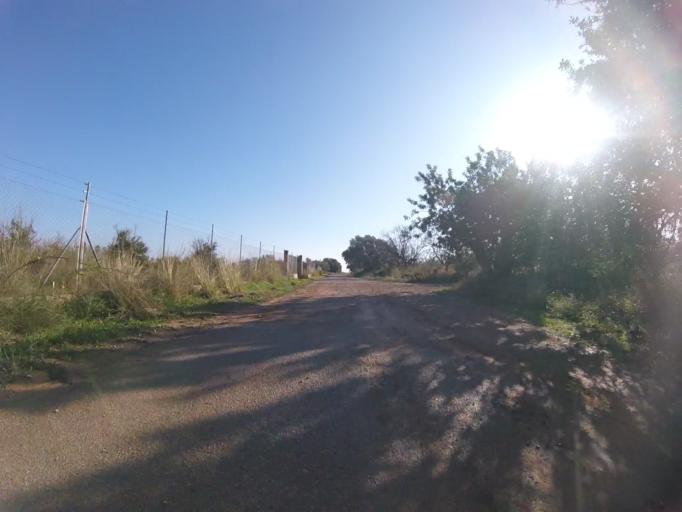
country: ES
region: Valencia
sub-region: Provincia de Castello
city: Peniscola
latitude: 40.3893
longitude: 0.3709
